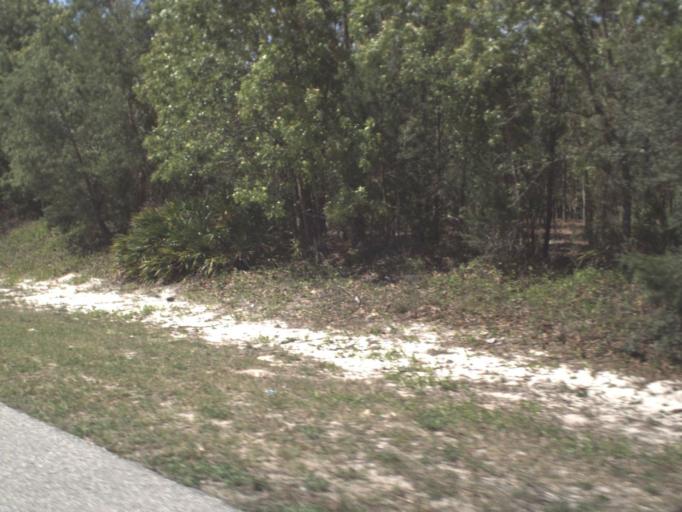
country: US
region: Florida
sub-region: Flagler County
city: Palm Coast
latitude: 29.6413
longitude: -81.2857
